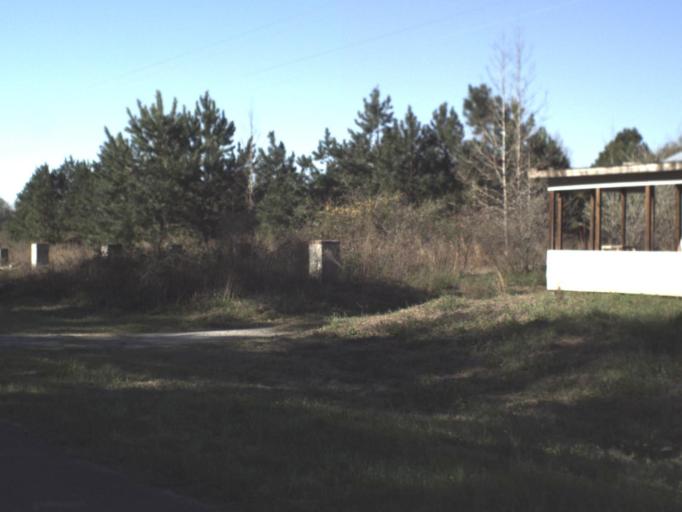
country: US
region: Georgia
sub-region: Brooks County
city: Quitman
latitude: 30.5666
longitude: -83.6374
